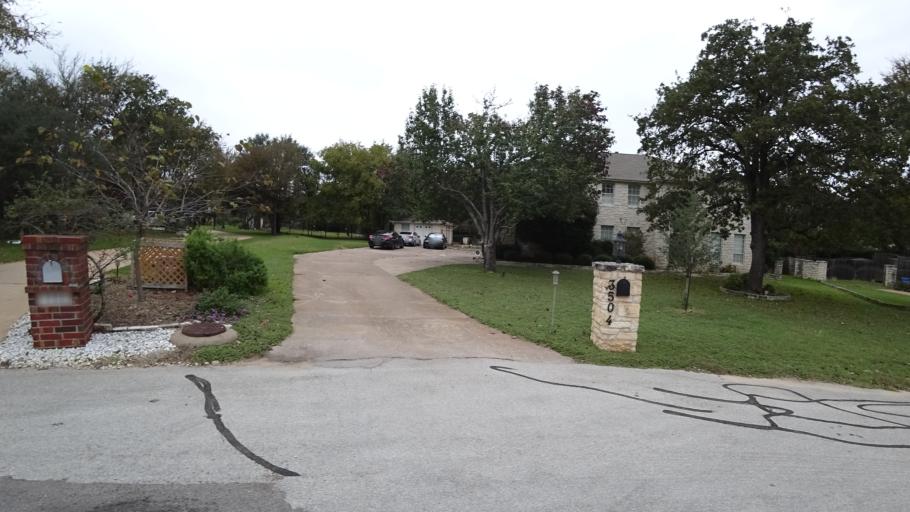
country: US
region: Texas
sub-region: Travis County
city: Shady Hollow
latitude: 30.1570
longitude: -97.8693
